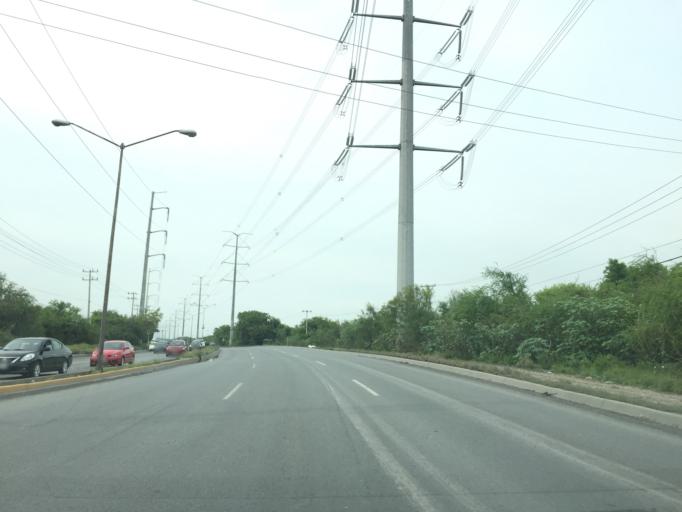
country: MX
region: Nuevo Leon
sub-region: Apodaca
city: Fraccionamiento Cosmopolis Octavo Sector
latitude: 25.7875
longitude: -100.2234
